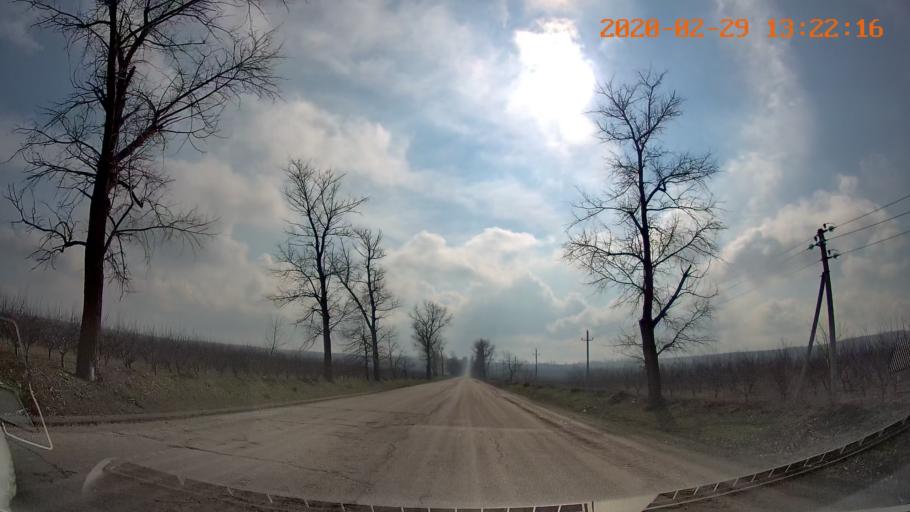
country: MD
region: Telenesti
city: Camenca
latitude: 47.9623
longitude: 28.6282
